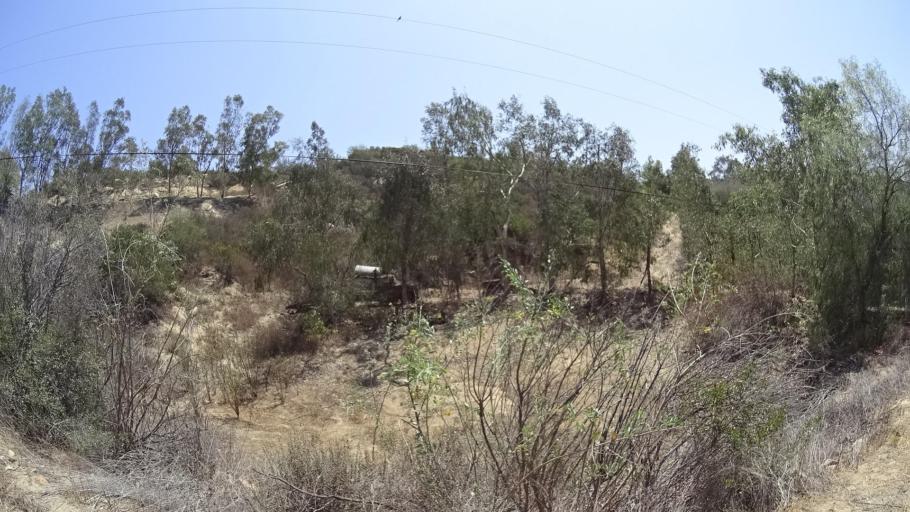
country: US
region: California
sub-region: San Diego County
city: Fallbrook
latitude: 33.4440
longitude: -117.2813
